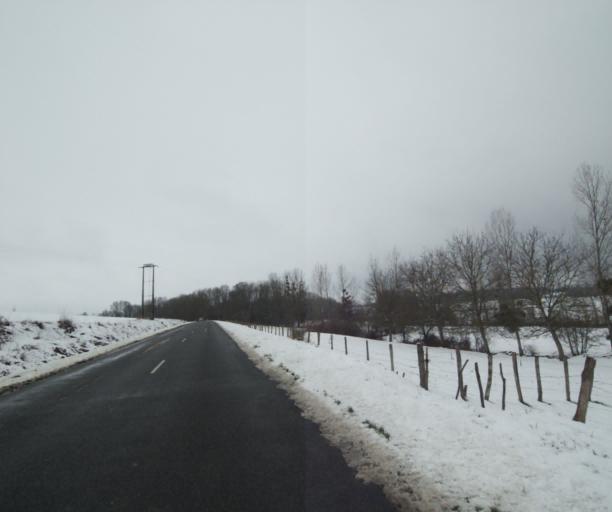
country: FR
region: Champagne-Ardenne
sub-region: Departement de la Haute-Marne
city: Wassy
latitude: 48.4441
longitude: 4.9559
